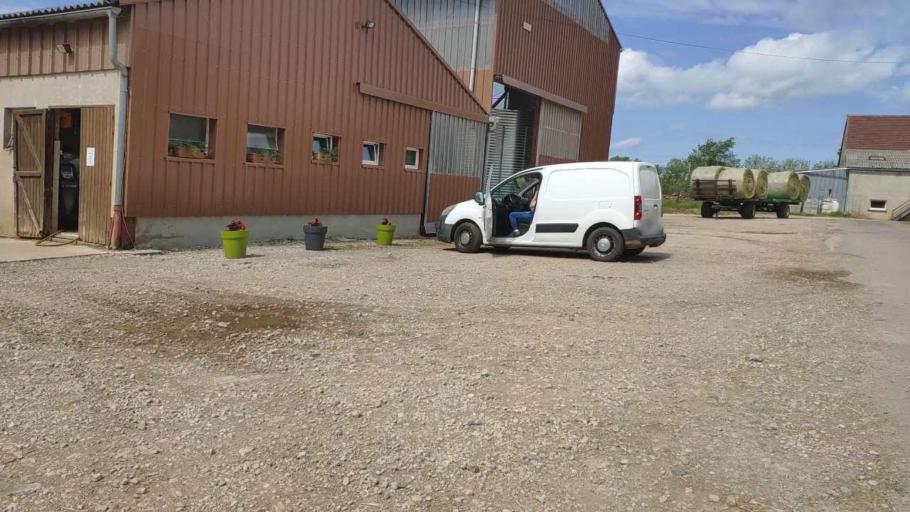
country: FR
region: Franche-Comte
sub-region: Departement du Jura
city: Poligny
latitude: 46.7713
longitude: 5.6301
